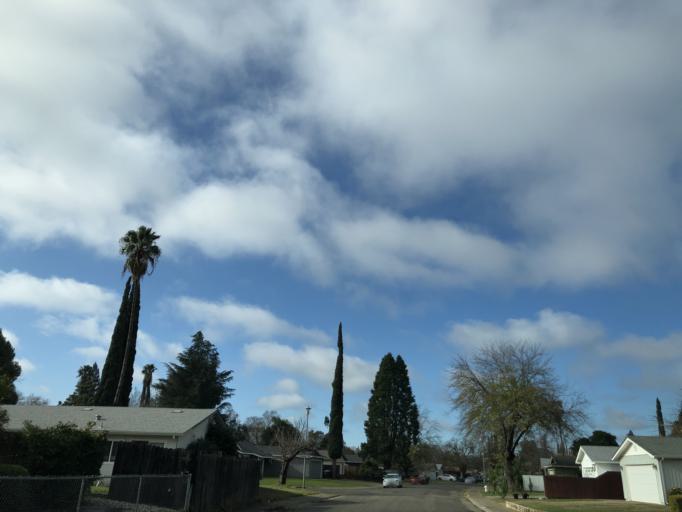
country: US
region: California
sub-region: Sacramento County
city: Rosemont
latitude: 38.5609
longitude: -121.3742
